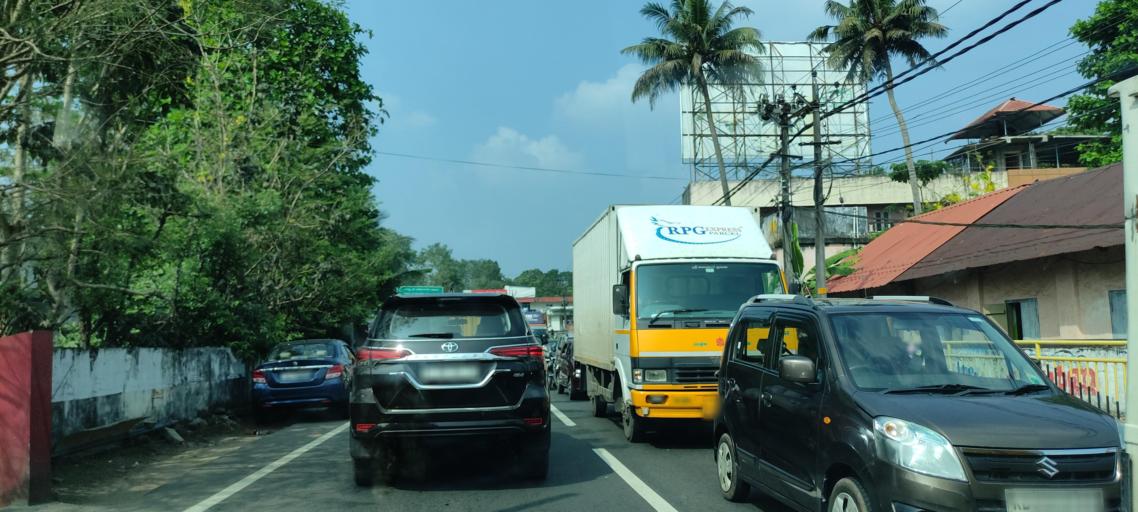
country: IN
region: Kerala
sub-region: Pattanamtitta
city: Adur
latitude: 9.2276
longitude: 76.6779
